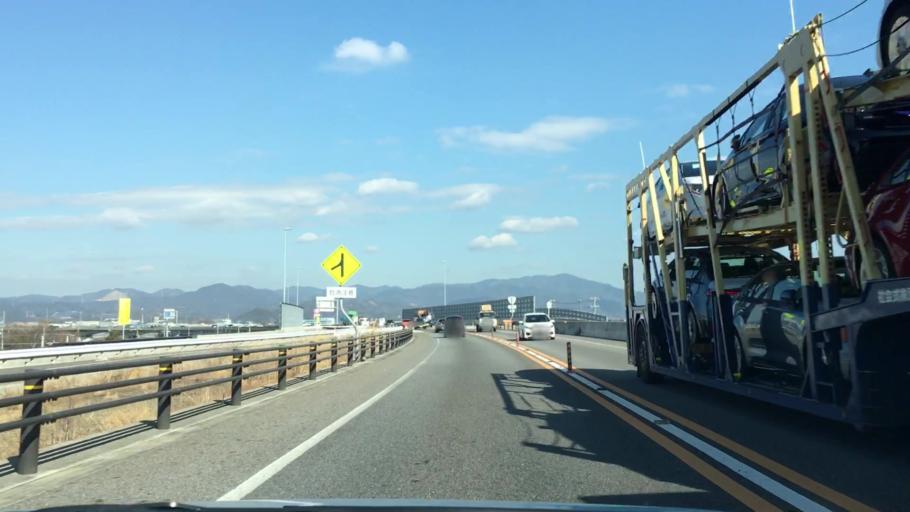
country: JP
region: Aichi
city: Kozakai-cho
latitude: 34.8029
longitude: 137.3365
